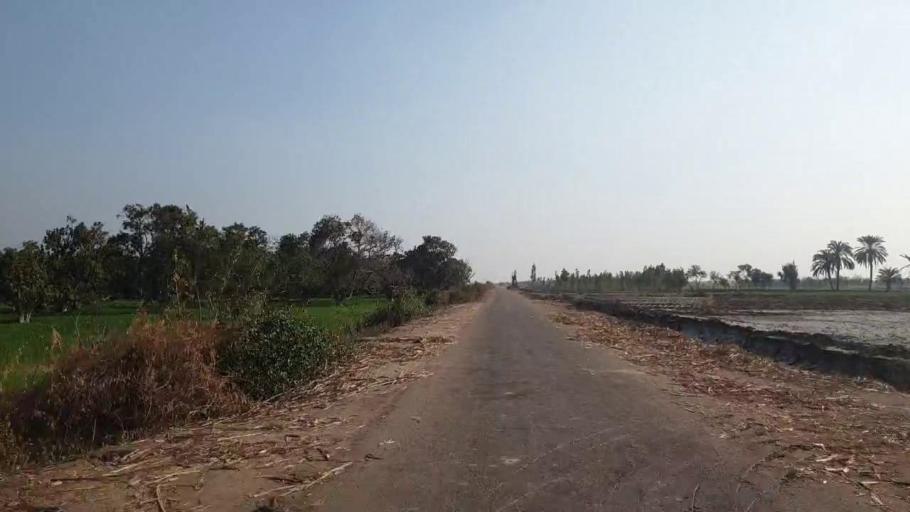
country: PK
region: Sindh
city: Tando Allahyar
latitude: 25.5954
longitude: 68.6186
